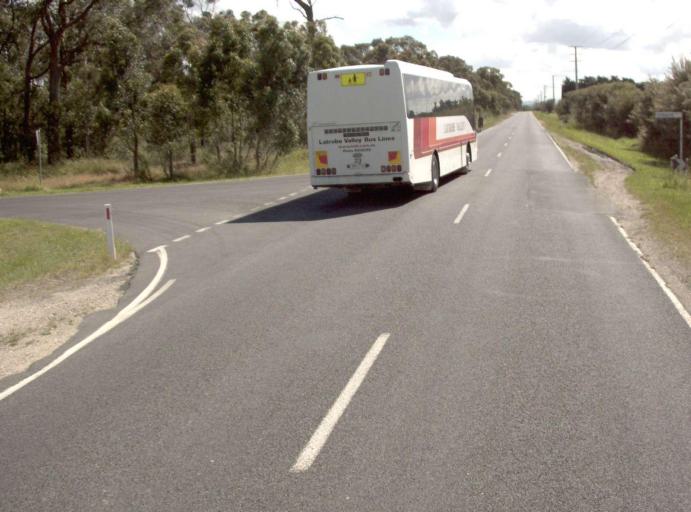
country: AU
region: Victoria
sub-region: Latrobe
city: Traralgon
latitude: -38.1329
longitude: 146.5521
